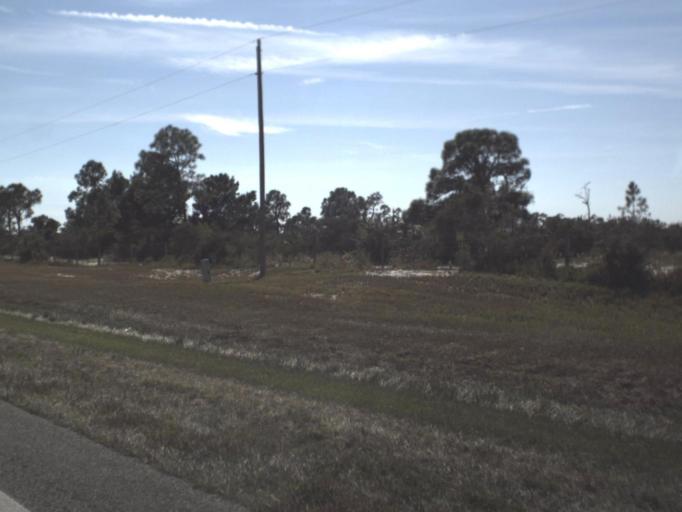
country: US
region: Florida
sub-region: Highlands County
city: Placid Lakes
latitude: 27.0940
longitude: -81.3337
